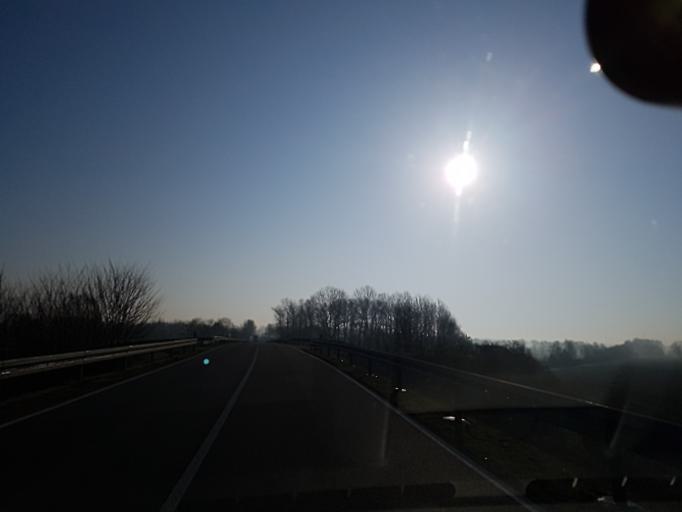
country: DE
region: Brandenburg
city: Bronkow
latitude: 51.6507
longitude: 13.8872
